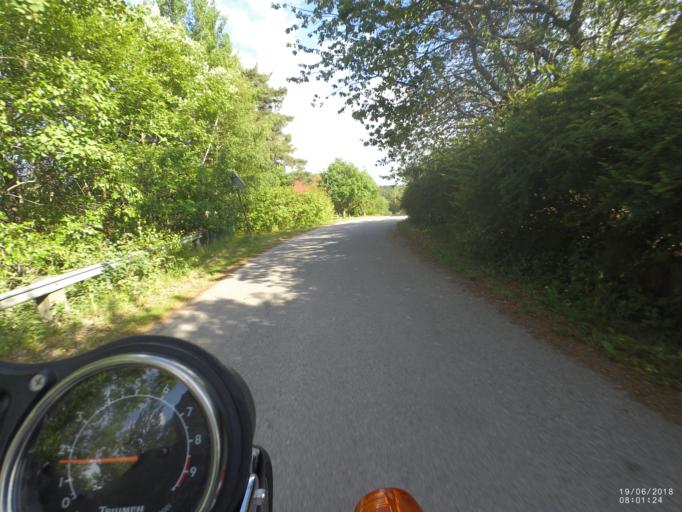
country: SE
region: Soedermanland
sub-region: Nykopings Kommun
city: Nykoping
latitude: 58.7760
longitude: 16.9982
